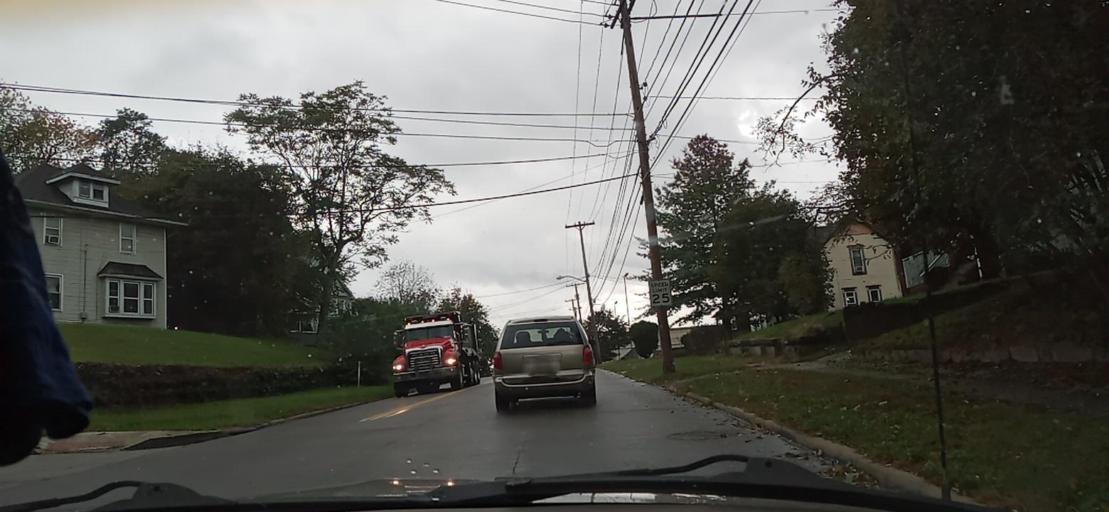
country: US
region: Ohio
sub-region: Summit County
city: Akron
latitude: 41.0911
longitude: -81.5240
